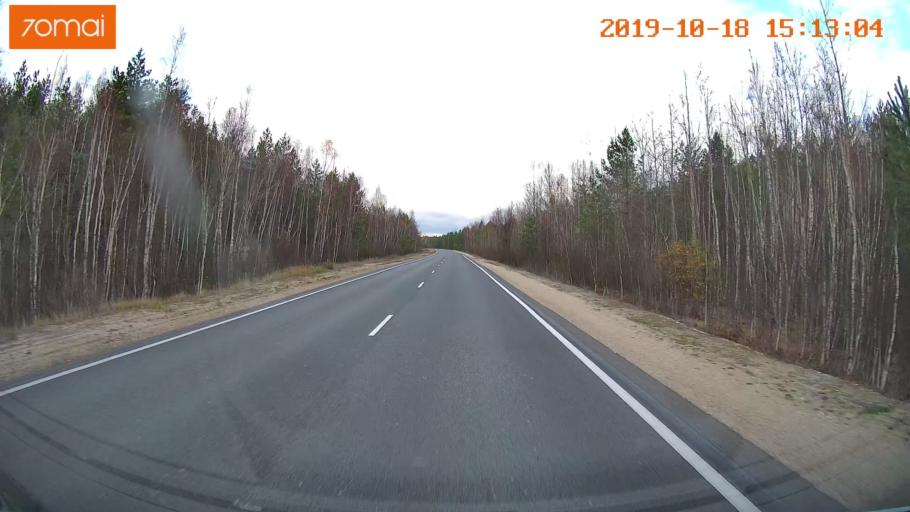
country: RU
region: Vladimir
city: Gus'-Khrustal'nyy
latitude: 55.5818
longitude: 40.7116
